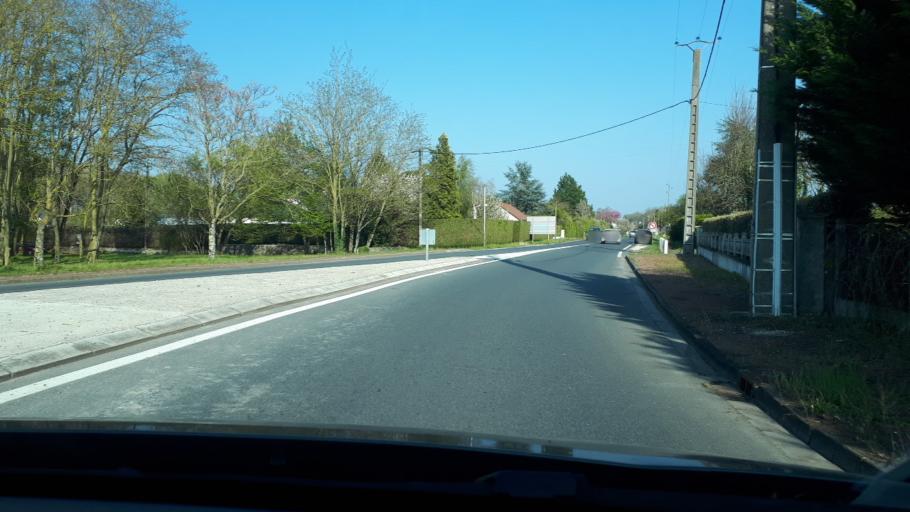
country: FR
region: Centre
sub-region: Departement d'Indre-et-Loire
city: Civray-de-Touraine
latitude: 47.3220
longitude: 1.0359
